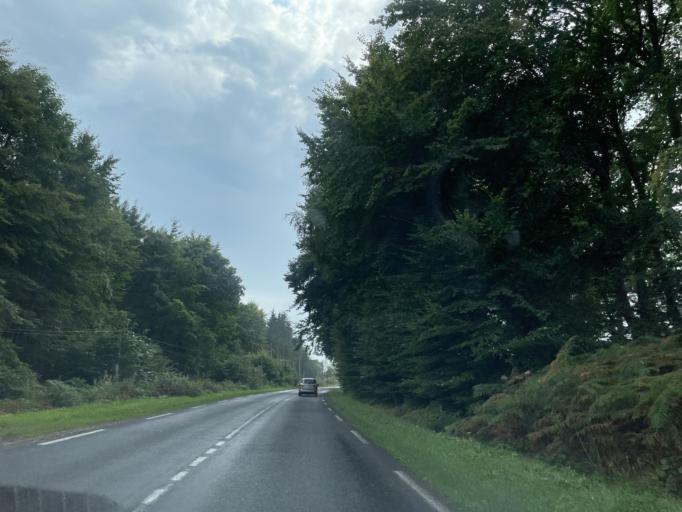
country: FR
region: Haute-Normandie
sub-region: Departement de la Seine-Maritime
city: Neufchatel-en-Bray
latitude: 49.7668
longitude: 1.4288
